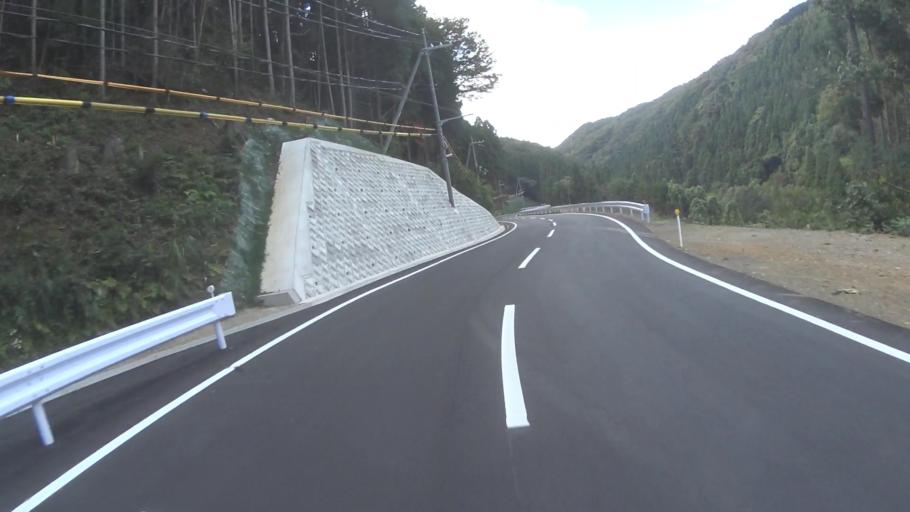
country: JP
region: Kyoto
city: Maizuru
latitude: 35.5578
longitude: 135.4346
